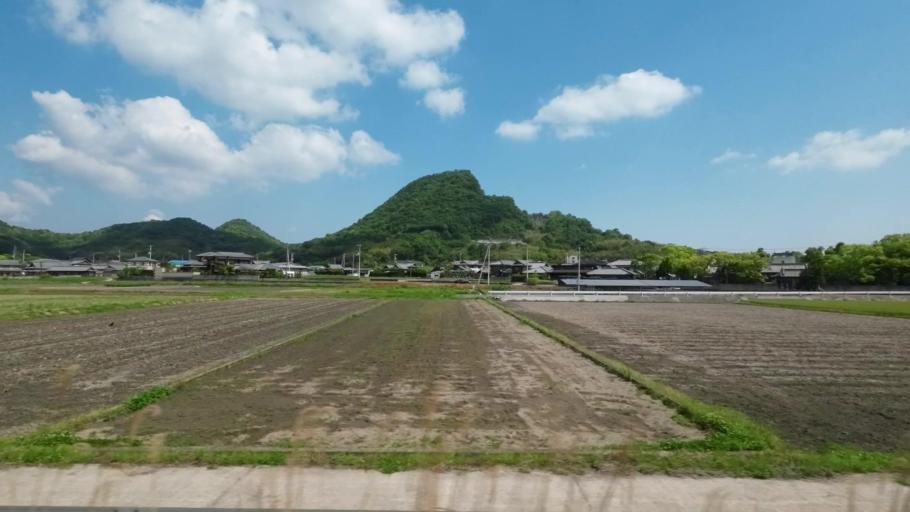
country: JP
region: Kagawa
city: Kan'onjicho
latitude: 34.1785
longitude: 133.7030
